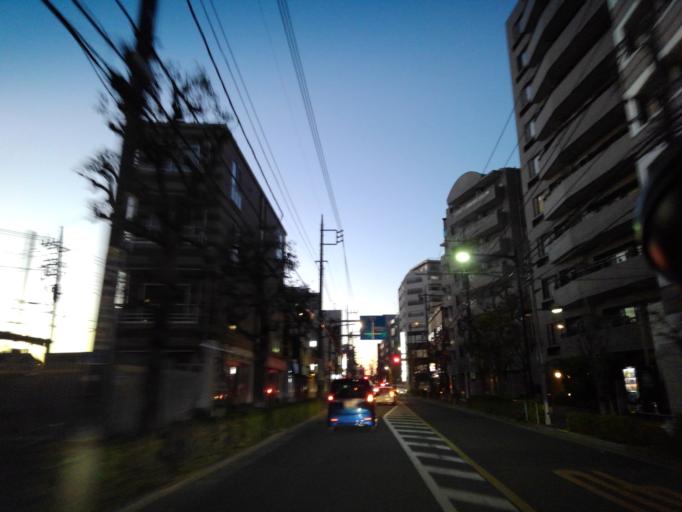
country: JP
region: Tokyo
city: Chofugaoka
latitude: 35.6482
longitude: 139.5442
